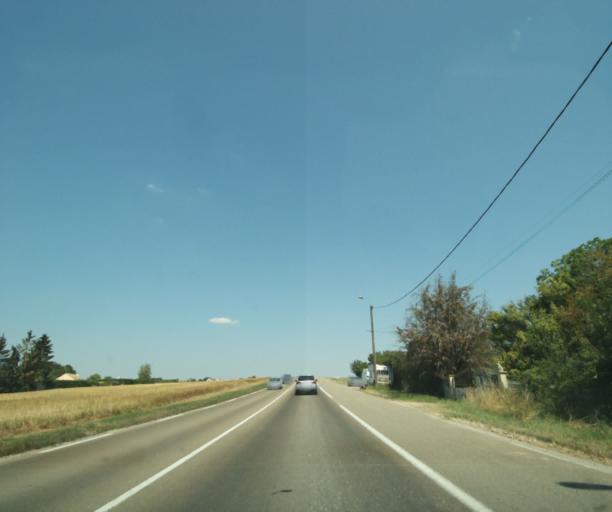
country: FR
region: Champagne-Ardenne
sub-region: Departement de la Marne
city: Sarry
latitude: 48.9069
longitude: 4.4344
